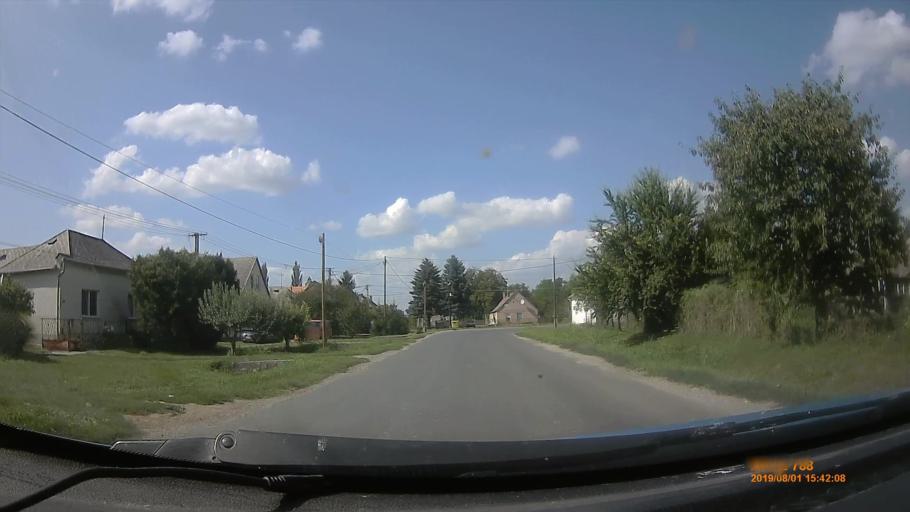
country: HU
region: Baranya
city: Szentlorinc
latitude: 45.9954
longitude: 17.9618
